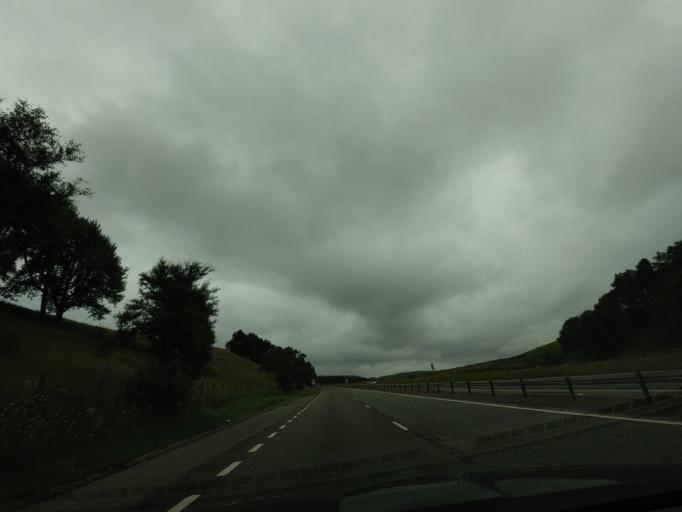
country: GB
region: Scotland
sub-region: Highland
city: Inverness
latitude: 57.4102
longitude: -4.1355
